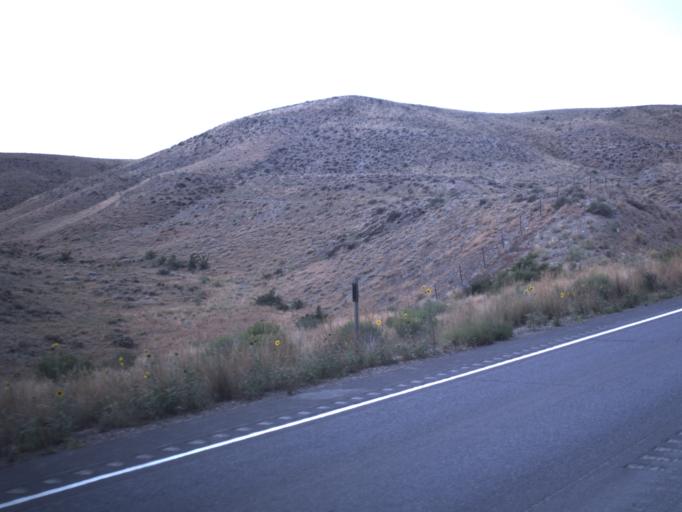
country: US
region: Utah
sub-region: Duchesne County
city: Duchesne
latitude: 40.1562
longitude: -110.2519
